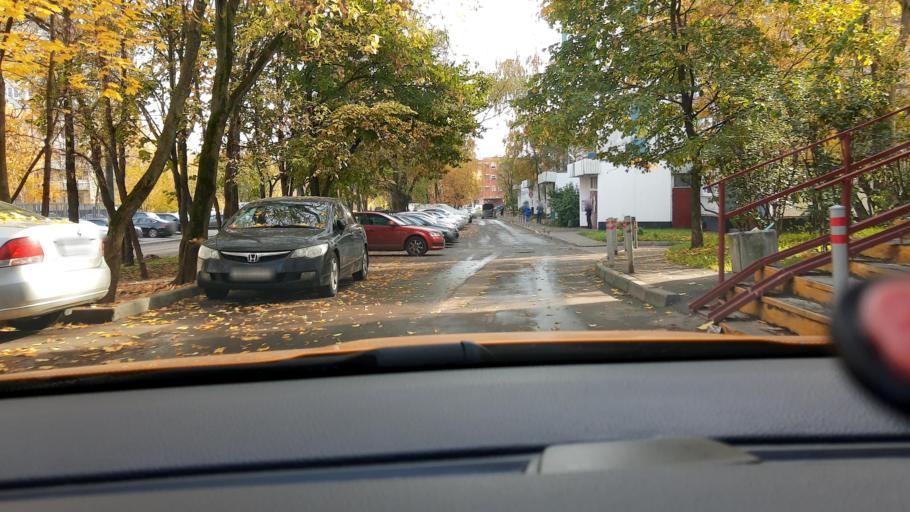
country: RU
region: Moscow
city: Babushkin
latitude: 55.8768
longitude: 37.7249
